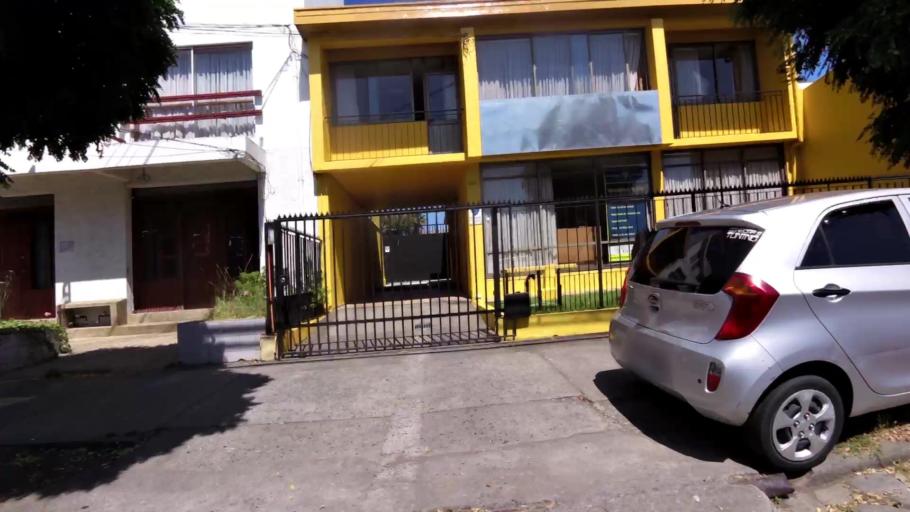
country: CL
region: Biobio
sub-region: Provincia de Concepcion
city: Concepcion
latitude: -36.8216
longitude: -73.0539
